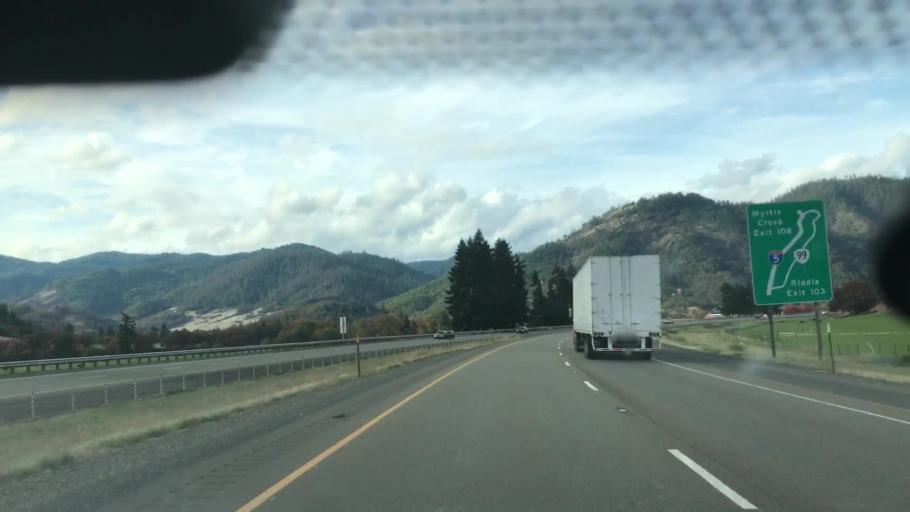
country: US
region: Oregon
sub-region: Douglas County
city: Tri-City
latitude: 42.9643
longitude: -123.3331
